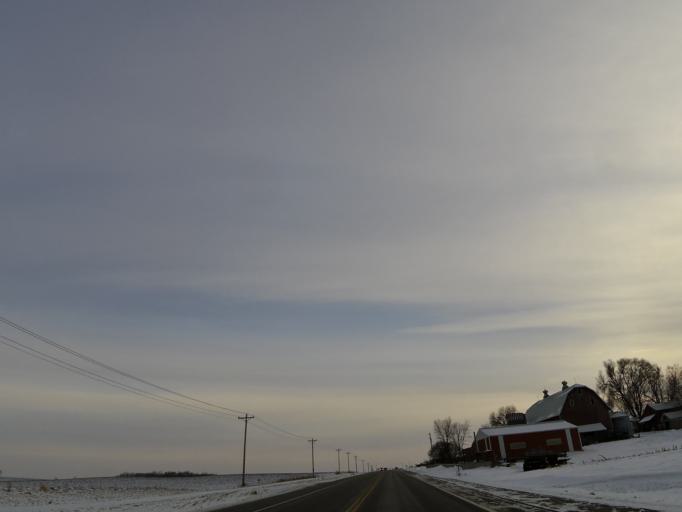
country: US
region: Minnesota
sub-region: Carver County
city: Carver
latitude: 44.7864
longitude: -93.6424
